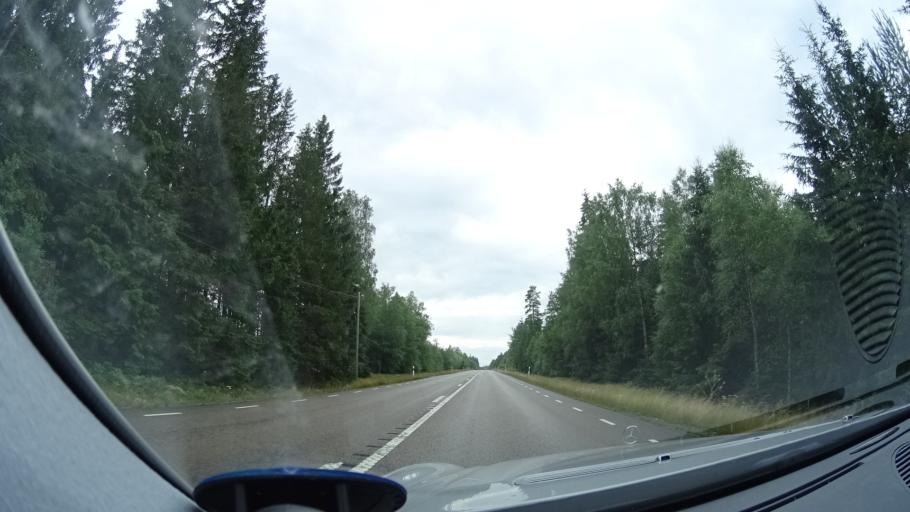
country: SE
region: Kronoberg
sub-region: Tingsryds Kommun
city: Tingsryd
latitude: 56.4539
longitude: 14.9946
